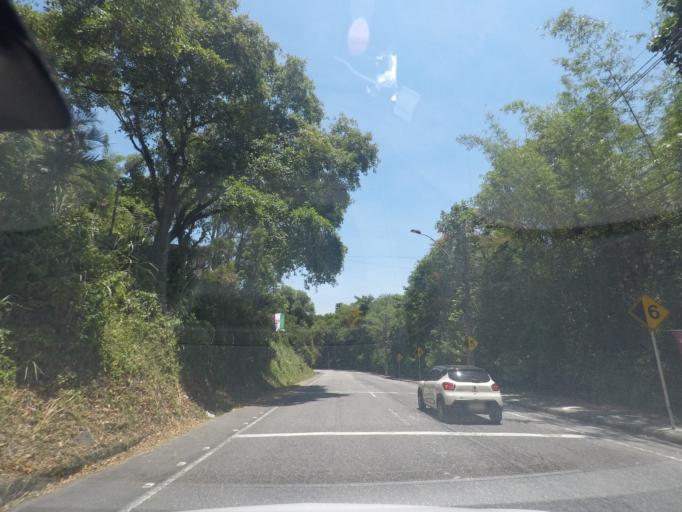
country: BR
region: Rio de Janeiro
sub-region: Niteroi
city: Niteroi
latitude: -22.9222
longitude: -43.0664
